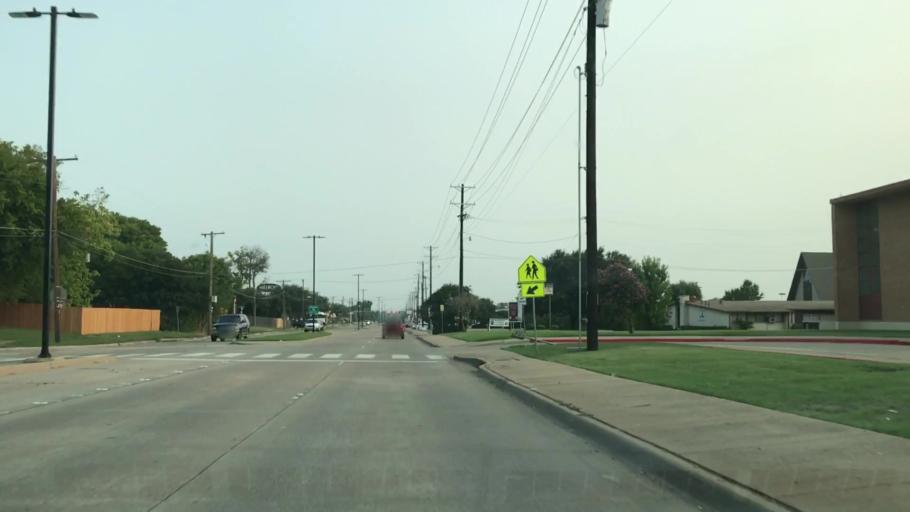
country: US
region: Texas
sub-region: Dallas County
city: Garland
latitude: 32.8827
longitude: -96.6310
